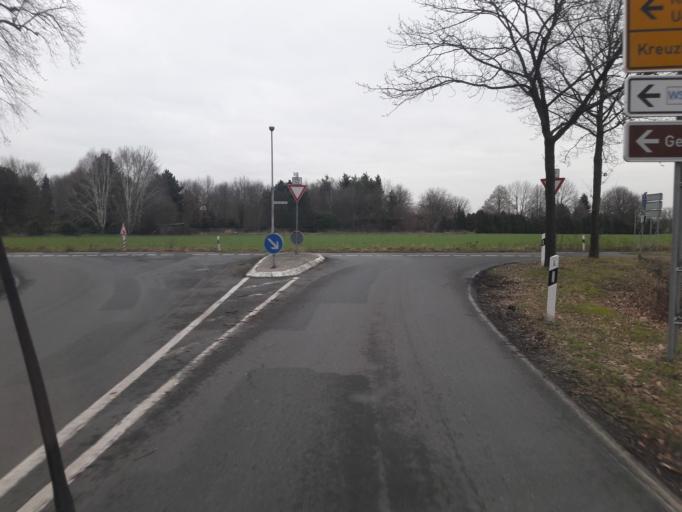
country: DE
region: Lower Saxony
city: Warmsen
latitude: 52.4513
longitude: 8.8531
